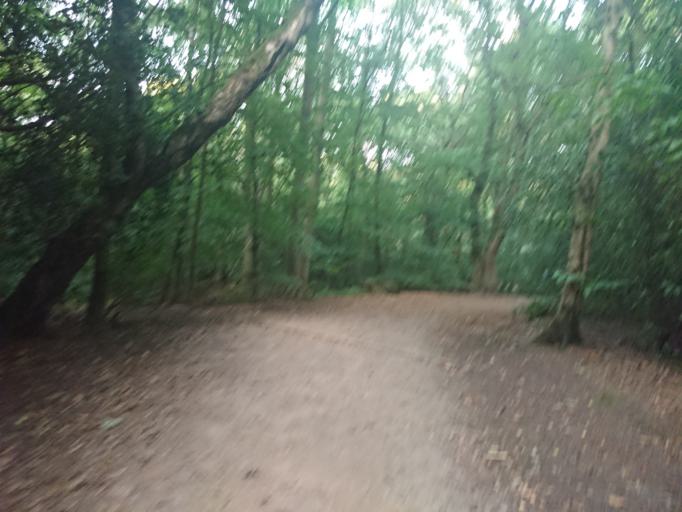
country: GB
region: England
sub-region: Derbyshire
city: Dronfield
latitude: 53.3445
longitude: -1.5146
